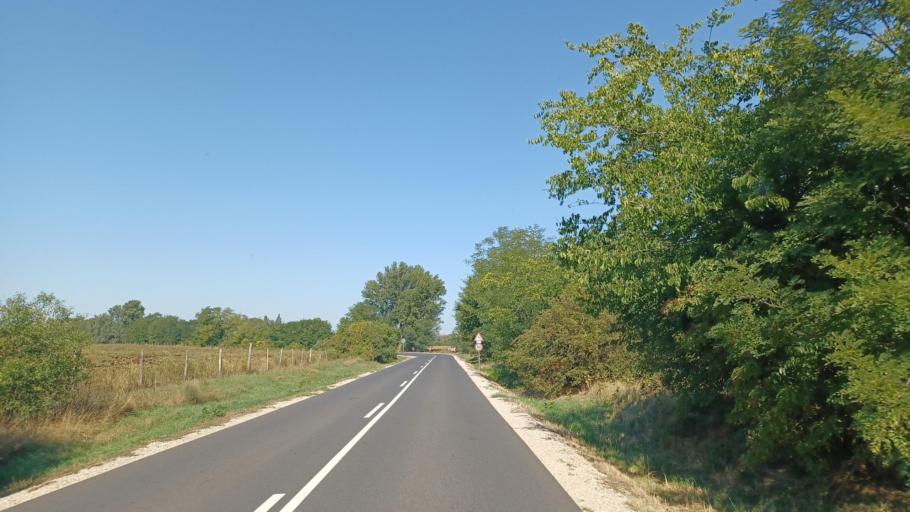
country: HU
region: Fejer
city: Alap
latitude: 46.7486
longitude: 18.6845
